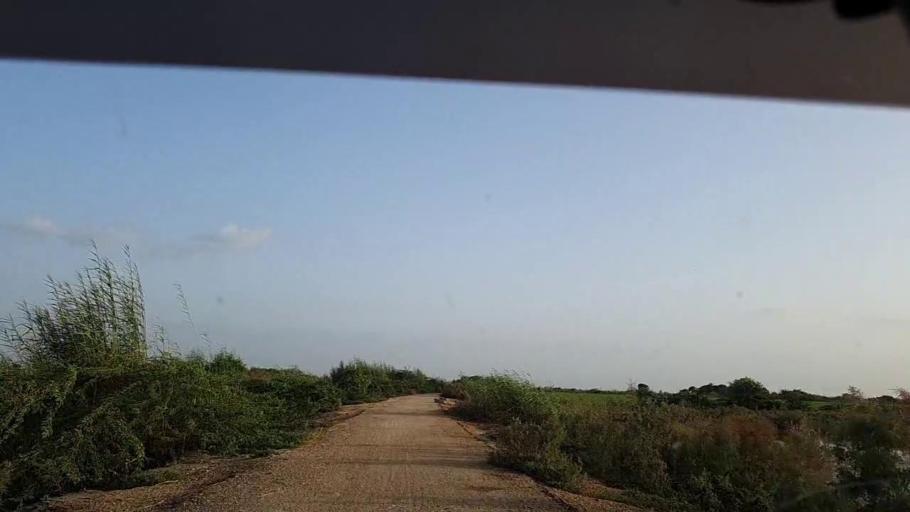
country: PK
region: Sindh
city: Kadhan
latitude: 24.5462
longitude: 68.9522
